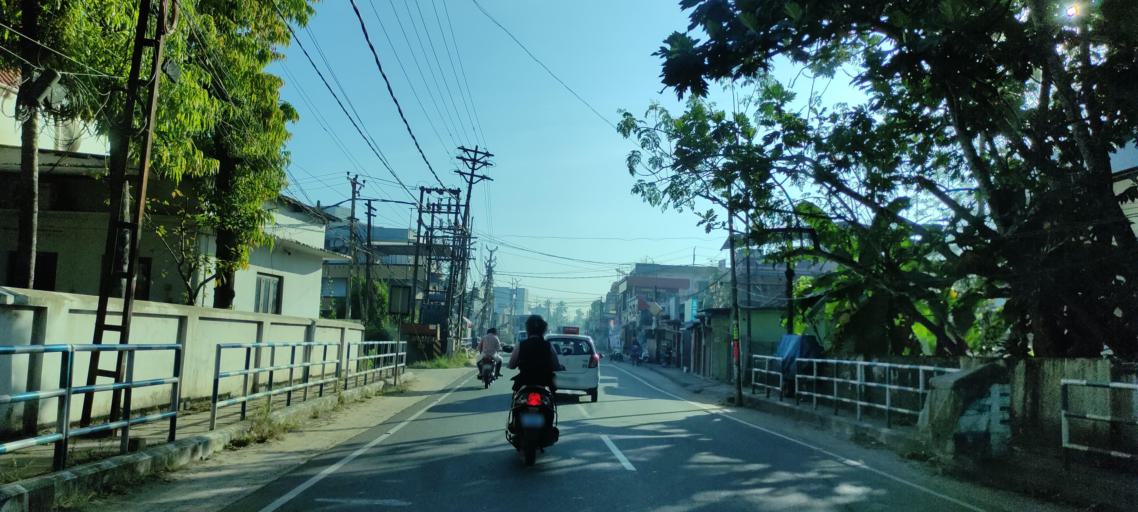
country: IN
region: Kerala
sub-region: Alappuzha
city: Kayankulam
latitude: 9.1755
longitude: 76.5064
